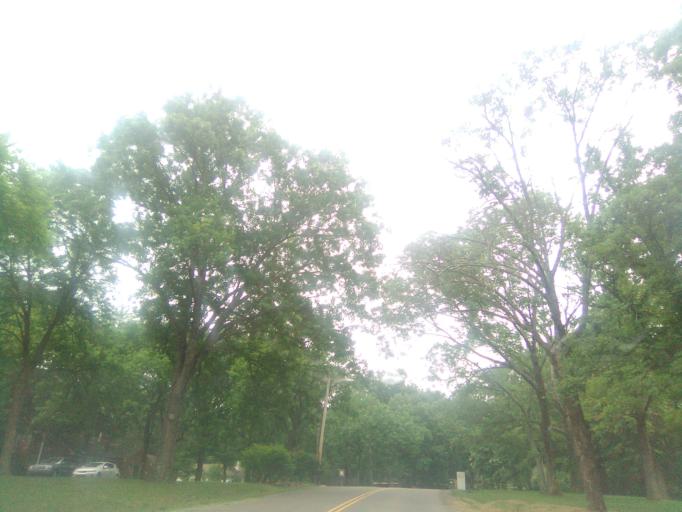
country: US
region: Tennessee
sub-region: Davidson County
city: Belle Meade
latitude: 36.1102
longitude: -86.8794
